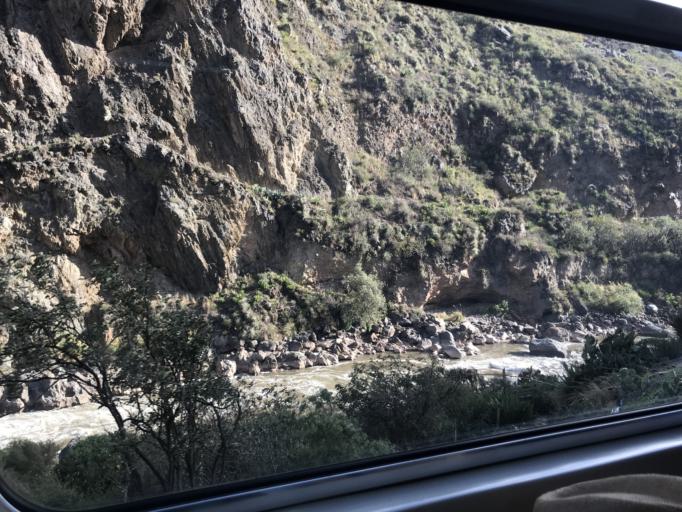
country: PE
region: Cusco
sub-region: Provincia de Urubamba
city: Ollantaytambo
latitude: -13.2152
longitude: -72.3828
